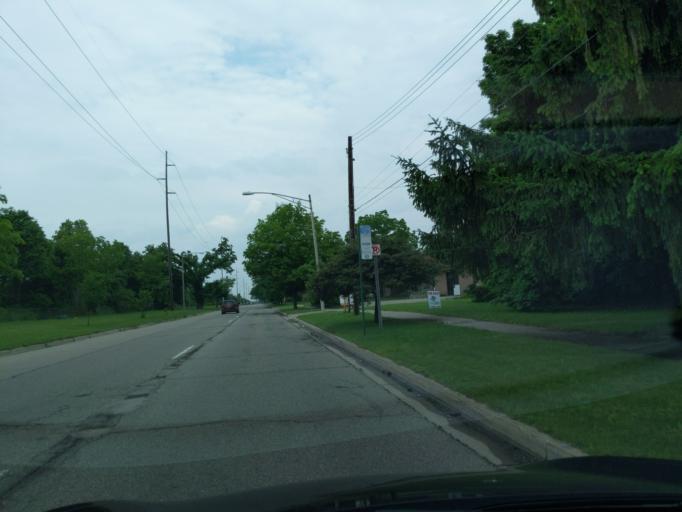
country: US
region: Michigan
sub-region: Ingham County
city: Lansing
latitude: 42.7256
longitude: -84.5771
